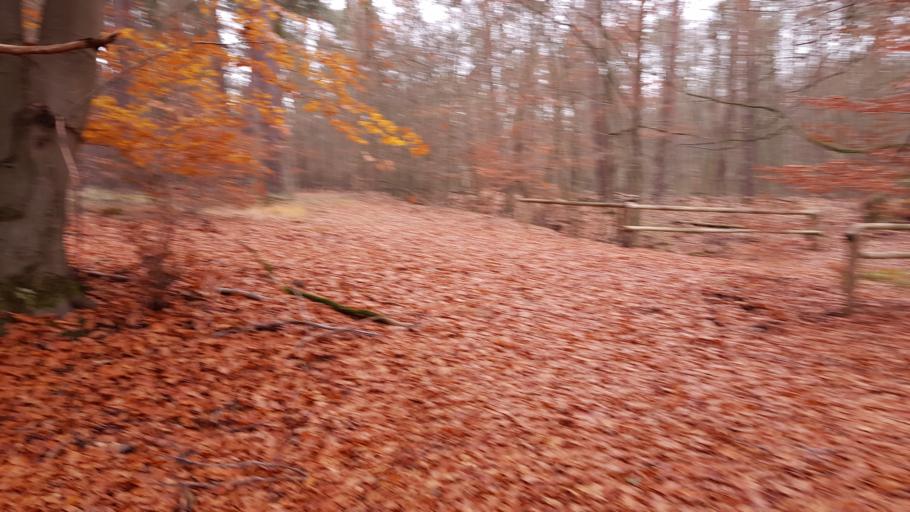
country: DE
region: Hesse
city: Raunheim
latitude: 49.9951
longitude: 8.4856
